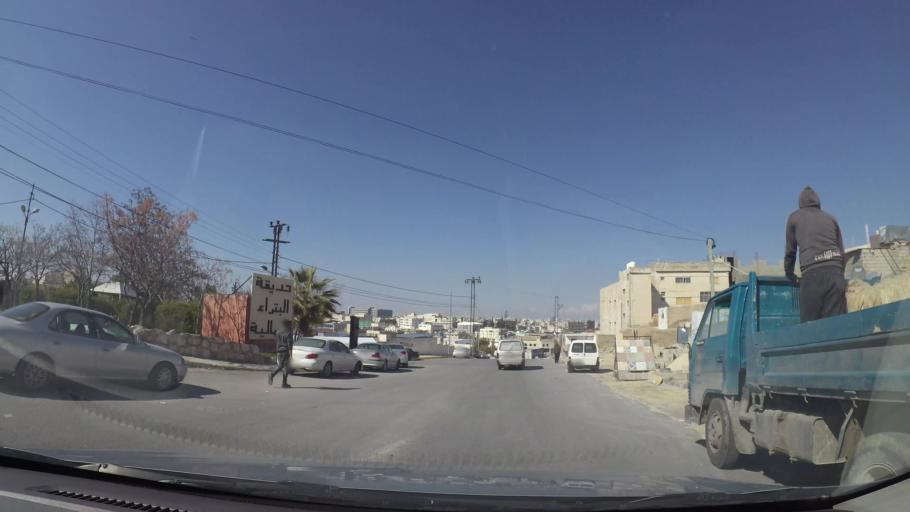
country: JO
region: Amman
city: Al Bunayyat ash Shamaliyah
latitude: 31.9118
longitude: 35.9017
